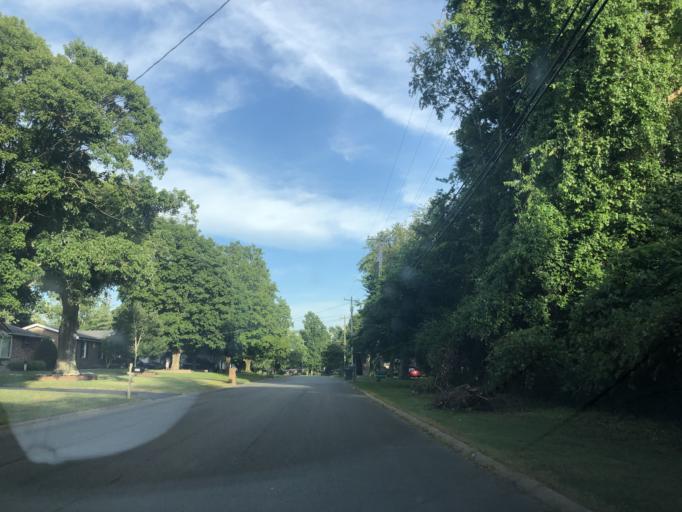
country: US
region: Tennessee
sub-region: Davidson County
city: Belle Meade
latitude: 36.0652
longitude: -86.9367
